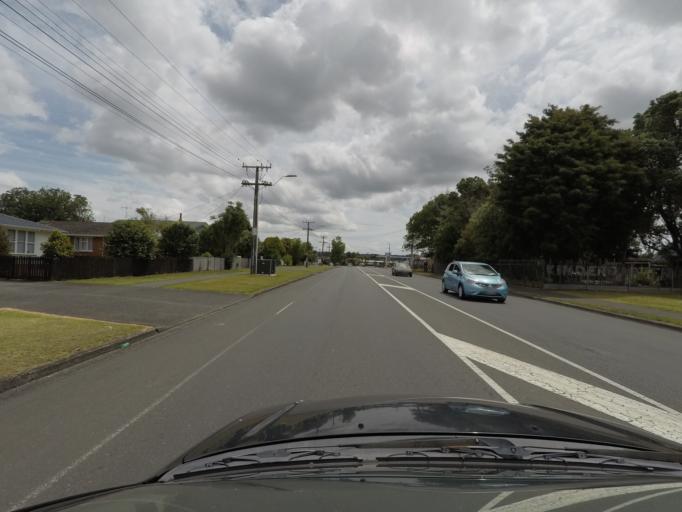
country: NZ
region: Northland
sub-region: Whangarei
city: Whangarei
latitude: -35.6844
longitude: 174.3305
